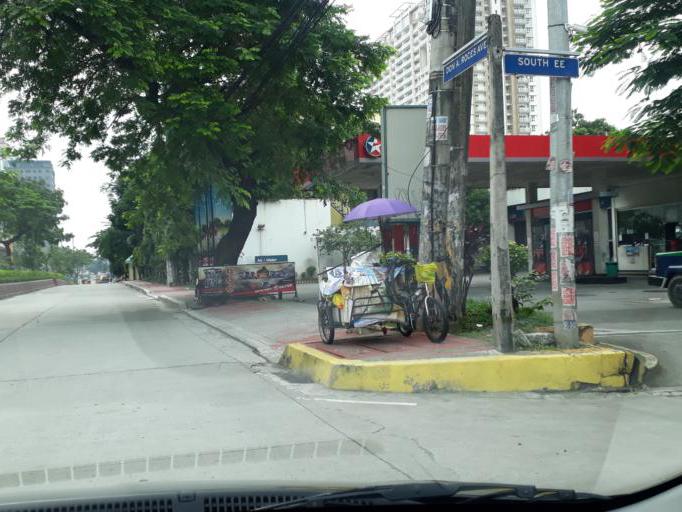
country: PH
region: Calabarzon
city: Del Monte
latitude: 14.6293
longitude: 121.0304
